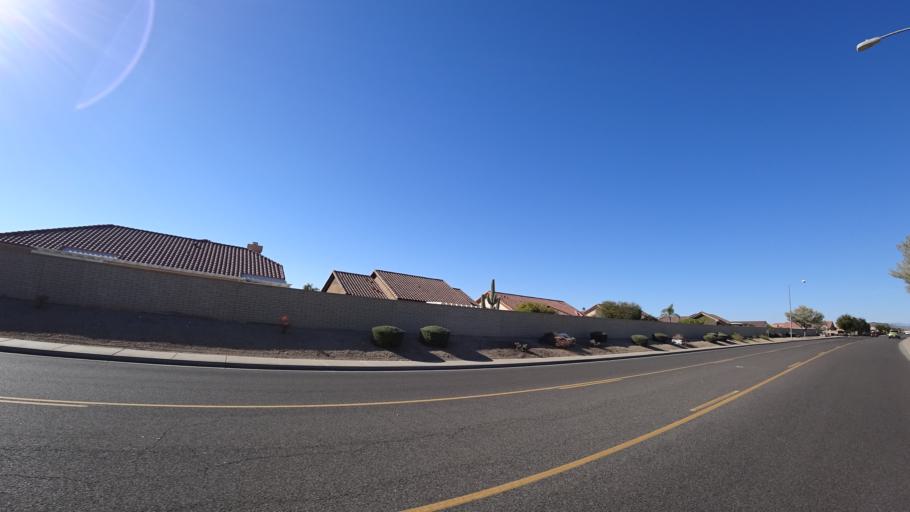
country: US
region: Arizona
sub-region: Maricopa County
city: Sun City West
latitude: 33.6807
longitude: -112.3814
